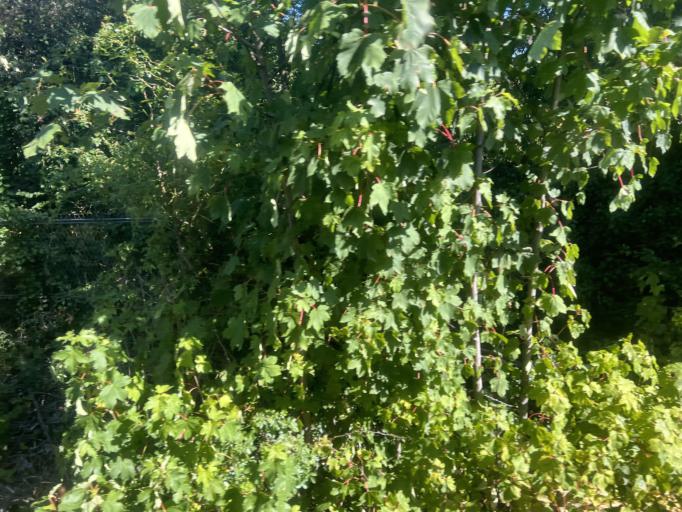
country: GB
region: England
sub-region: Lincolnshire
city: Heckington
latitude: 52.9776
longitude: -0.2957
